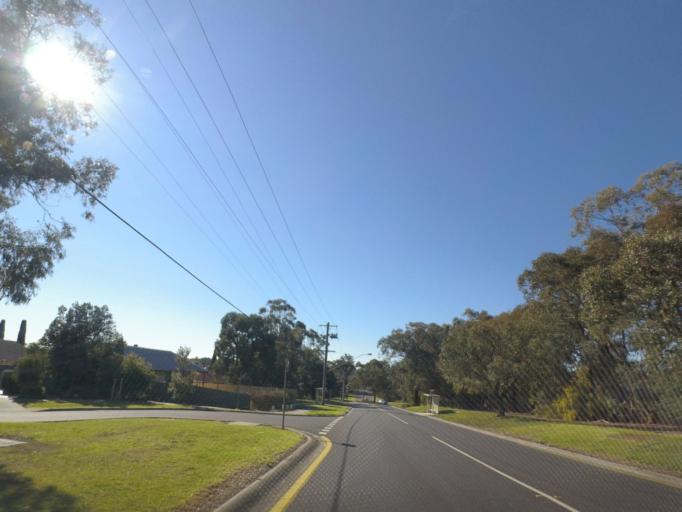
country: AU
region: Victoria
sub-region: Maroondah
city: Croydon Hills
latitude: -37.7757
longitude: 145.2753
